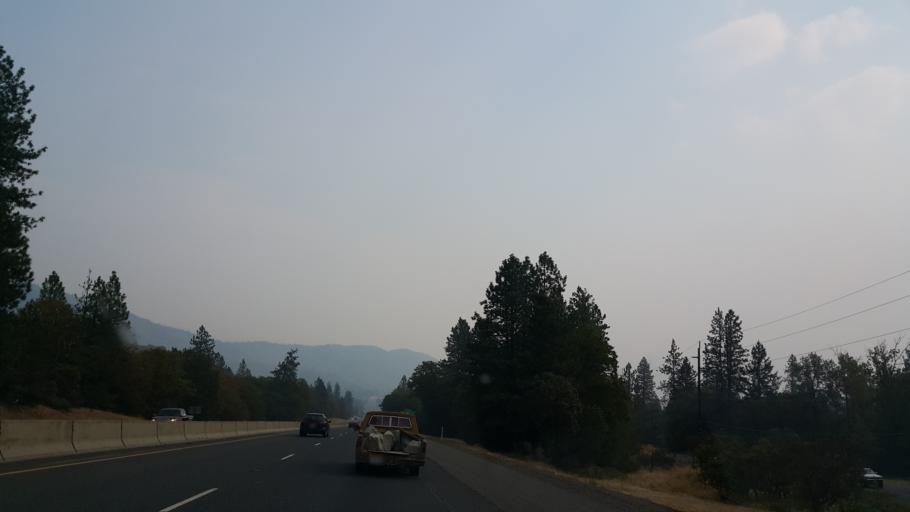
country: US
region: Oregon
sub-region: Josephine County
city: Grants Pass
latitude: 42.4755
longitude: -123.3474
